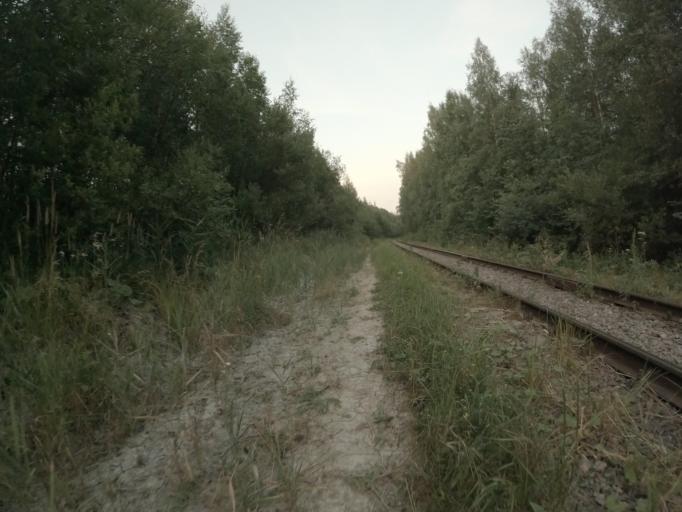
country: RU
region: St.-Petersburg
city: Krasnogvargeisky
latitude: 59.9430
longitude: 30.5303
